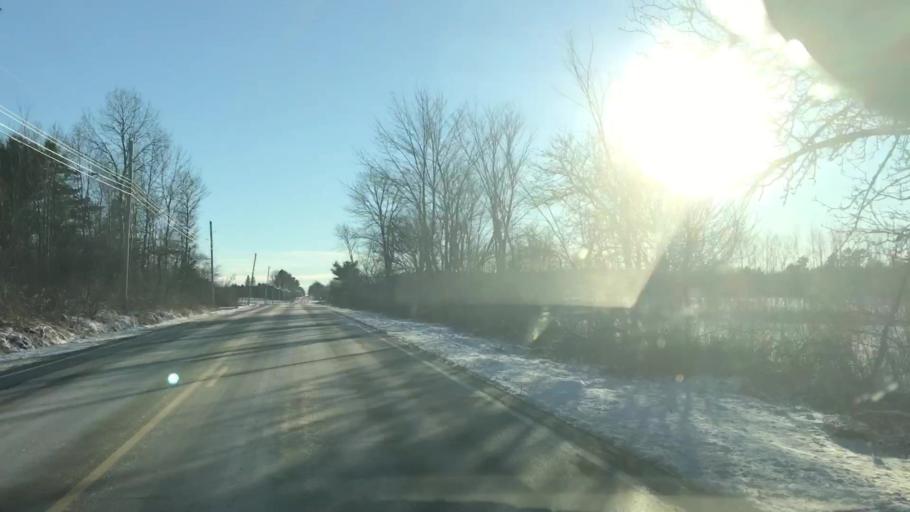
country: US
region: New Hampshire
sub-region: Grafton County
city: Haverhill
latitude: 44.0069
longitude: -72.0714
